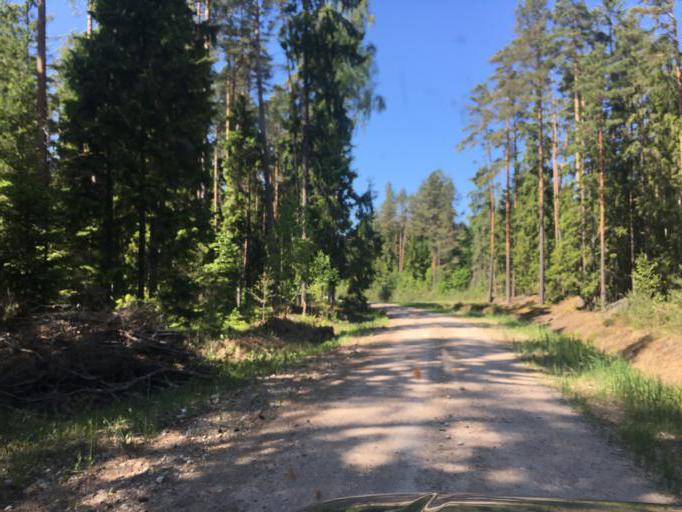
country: LV
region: Talsu Rajons
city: Valdemarpils
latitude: 57.4430
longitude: 22.6645
